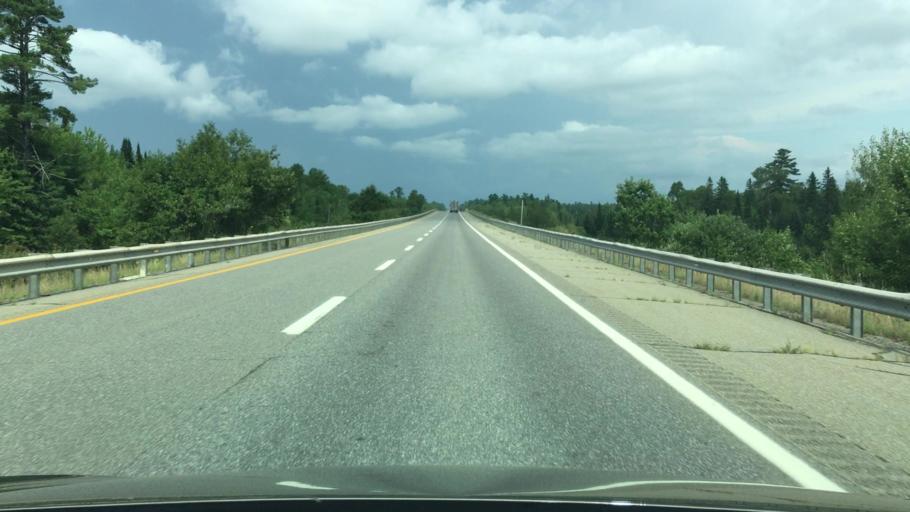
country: US
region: Maine
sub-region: Penobscot County
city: Lincoln
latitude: 45.3916
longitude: -68.6019
